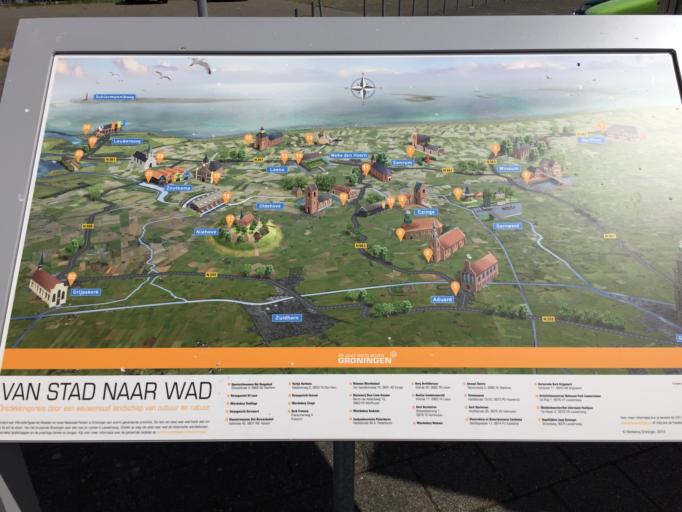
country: NL
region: Friesland
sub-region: Gemeente Dongeradeel
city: Anjum
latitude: 53.4100
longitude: 6.1966
